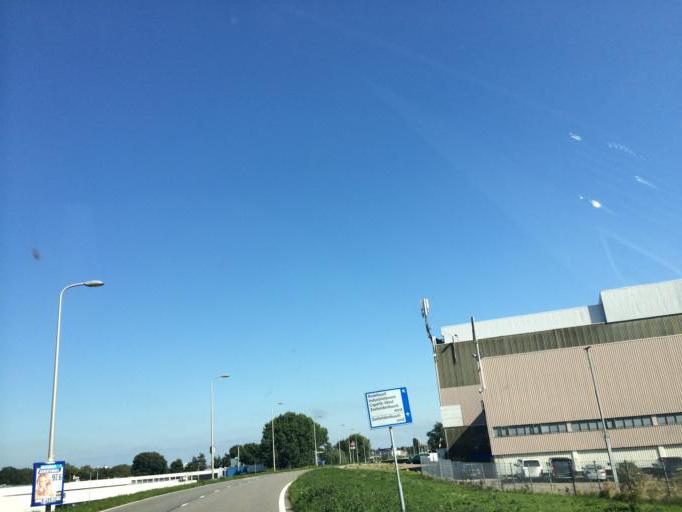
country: NL
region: South Holland
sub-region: Gemeente Rotterdam
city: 's-Gravenland
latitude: 51.9099
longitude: 4.5542
